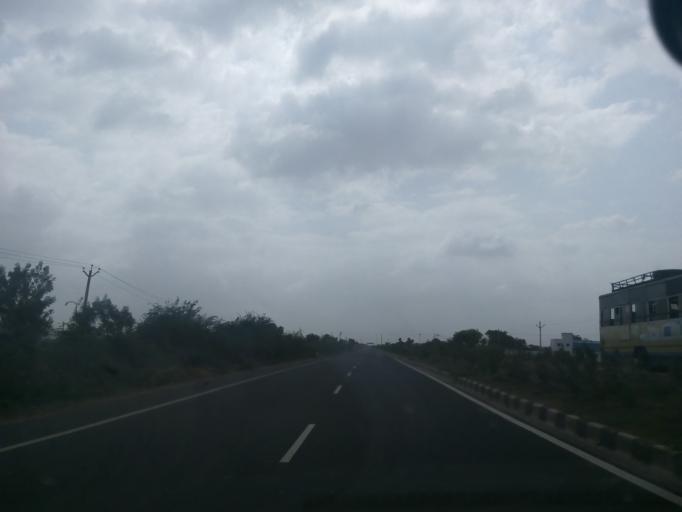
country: IN
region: Gujarat
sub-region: Surendranagar
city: Halvad
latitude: 23.0047
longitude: 71.1508
